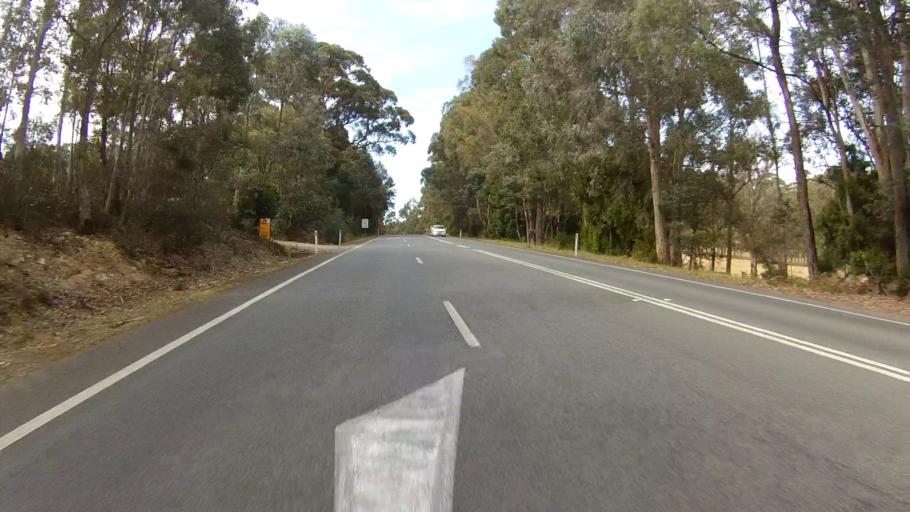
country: AU
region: Tasmania
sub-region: Kingborough
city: Kettering
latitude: -43.1102
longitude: 147.2423
